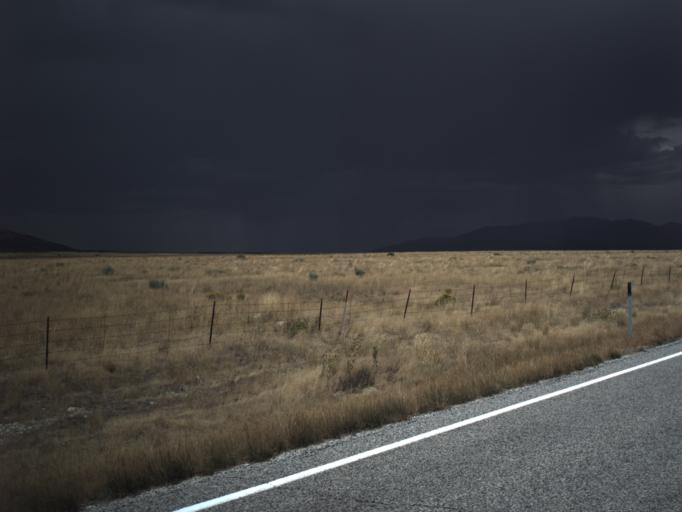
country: US
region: Idaho
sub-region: Oneida County
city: Malad City
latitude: 41.8769
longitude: -113.1196
